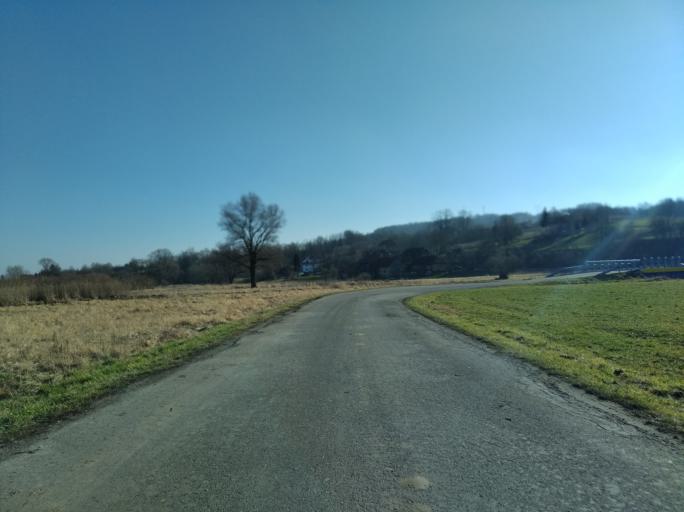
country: PL
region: Subcarpathian Voivodeship
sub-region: Powiat brzozowski
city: Domaradz
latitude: 49.8019
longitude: 21.9073
